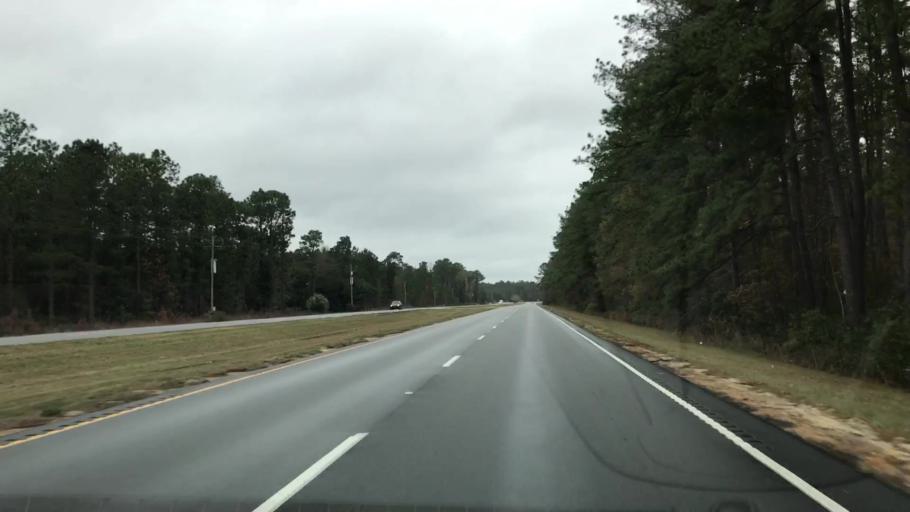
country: US
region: South Carolina
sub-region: Georgetown County
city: Georgetown
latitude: 33.2416
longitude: -79.3755
